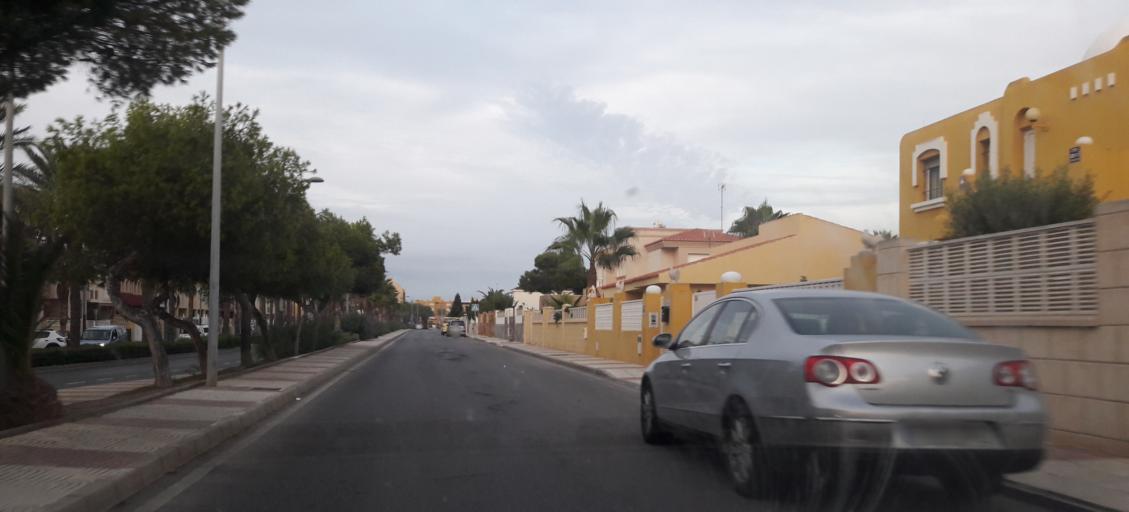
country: ES
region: Andalusia
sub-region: Provincia de Almeria
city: Roquetas de Mar
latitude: 36.7321
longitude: -2.6267
